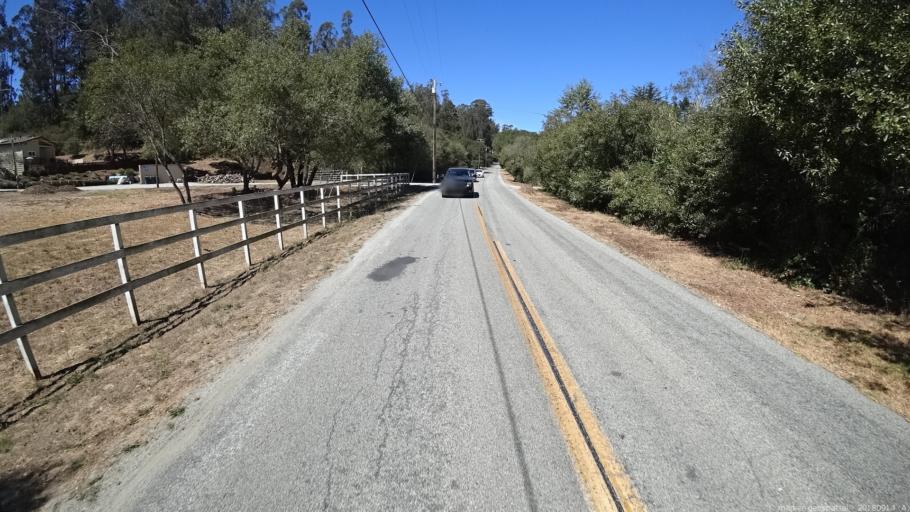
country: US
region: California
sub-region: Monterey County
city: Las Lomas
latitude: 36.8793
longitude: -121.6929
